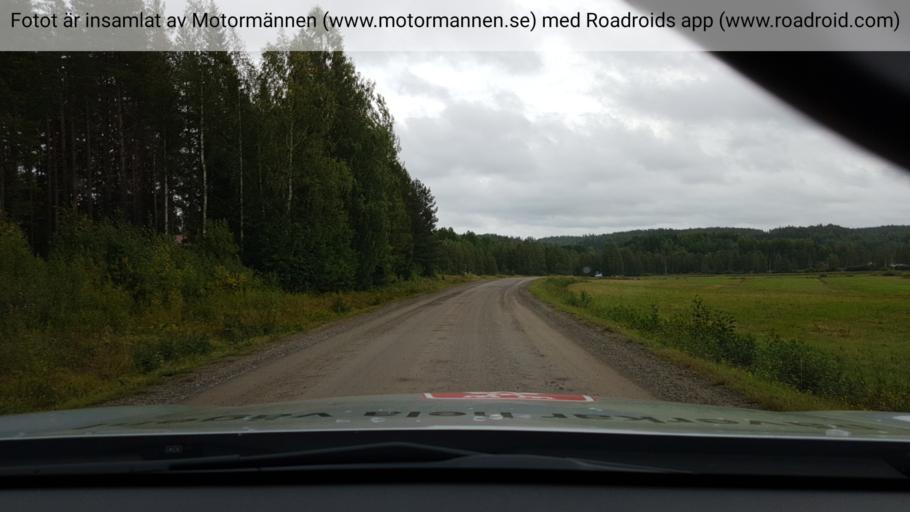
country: SE
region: Vaesterbotten
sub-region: Skelleftea Kommun
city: Burtraesk
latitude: 64.3142
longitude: 20.6520
